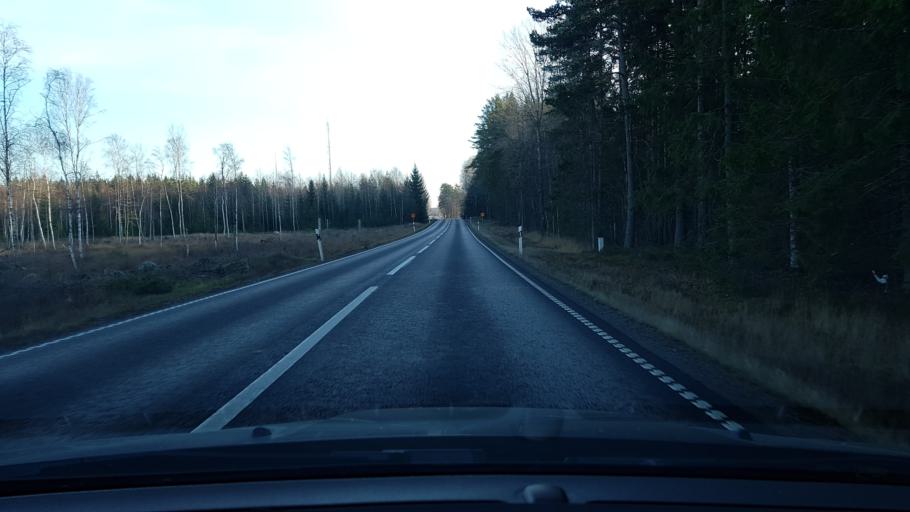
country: SE
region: Stockholm
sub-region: Norrtalje Kommun
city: Nykvarn
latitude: 59.7407
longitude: 18.2281
